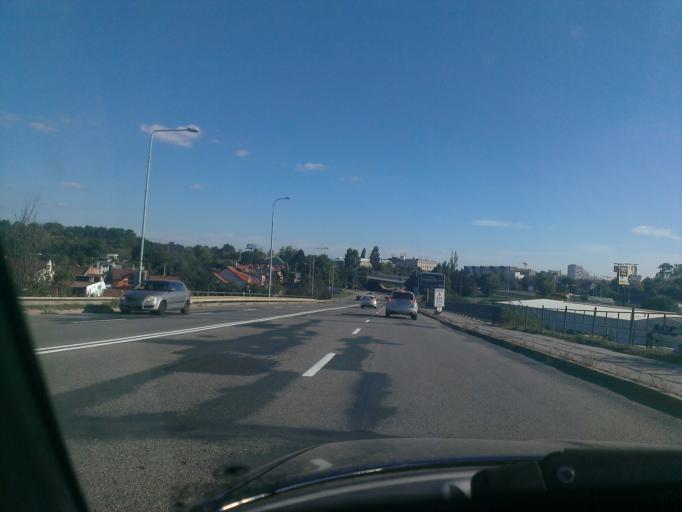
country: CZ
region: South Moravian
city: Podoli
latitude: 49.1879
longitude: 16.6650
